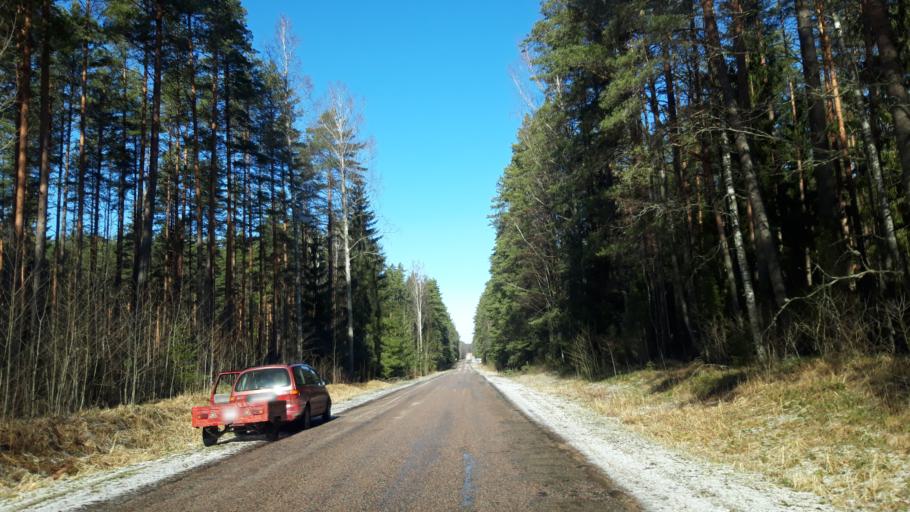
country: LV
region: Strenci
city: Strenci
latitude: 57.5965
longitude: 25.7185
